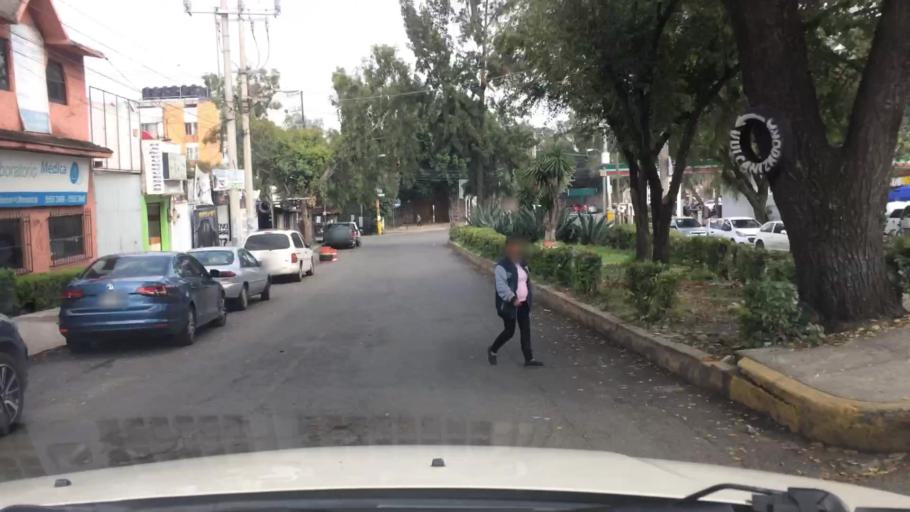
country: MX
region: Mexico City
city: Xochimilco
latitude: 19.2668
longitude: -99.1273
